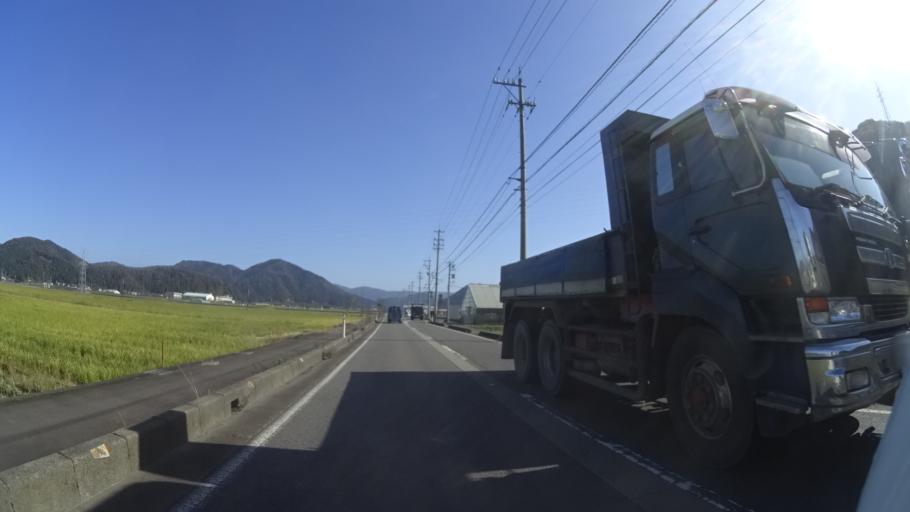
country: JP
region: Fukui
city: Sabae
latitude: 35.9483
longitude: 136.2216
